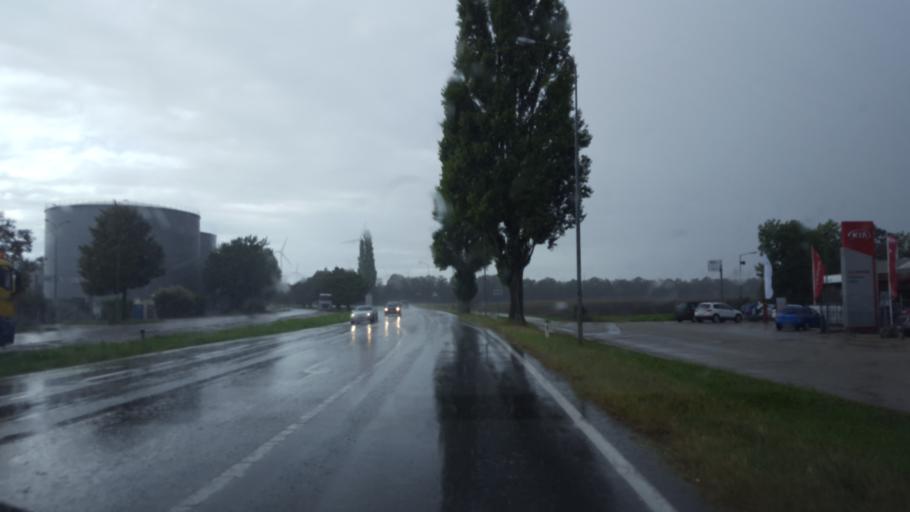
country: AT
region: Lower Austria
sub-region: Politischer Bezirk Bruck an der Leitha
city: Bruck an der Leitha
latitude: 48.0231
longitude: 16.7576
